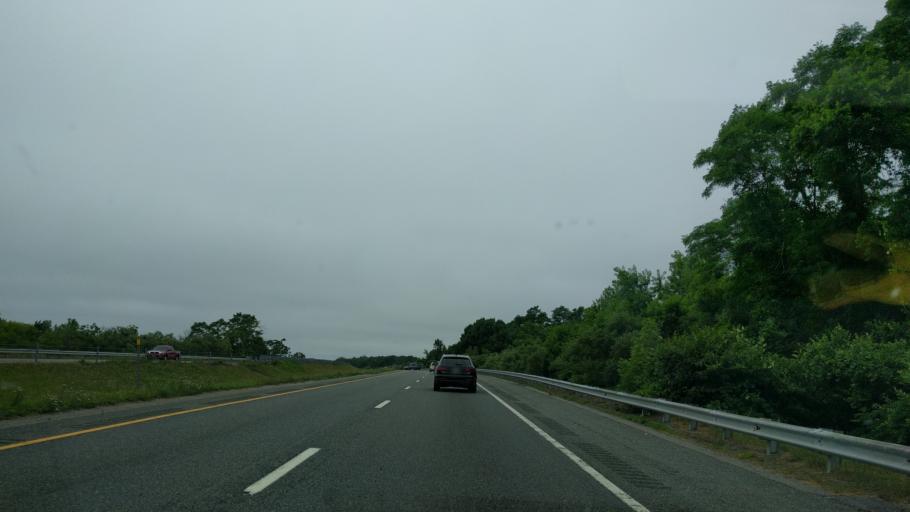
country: US
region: Rhode Island
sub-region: Washington County
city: Exeter
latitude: 41.6042
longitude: -71.4980
